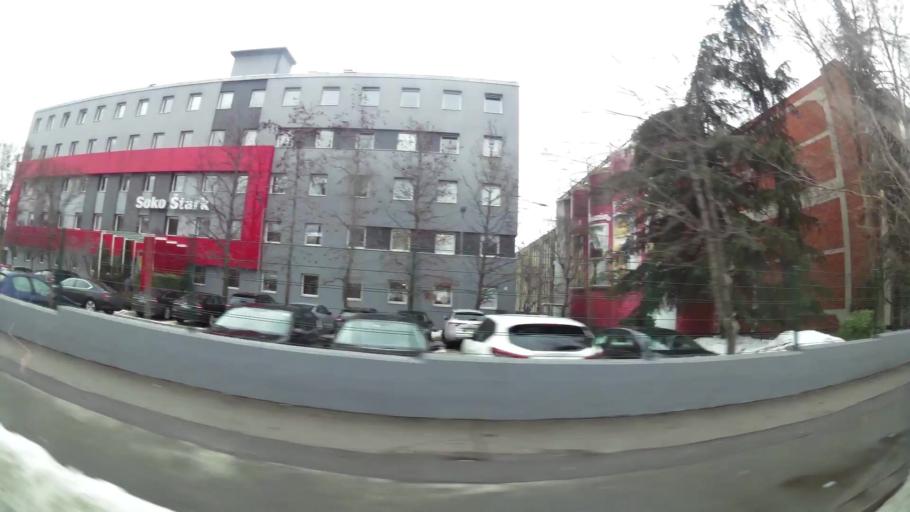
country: RS
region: Central Serbia
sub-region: Belgrade
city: Vozdovac
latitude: 44.7655
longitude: 20.4873
